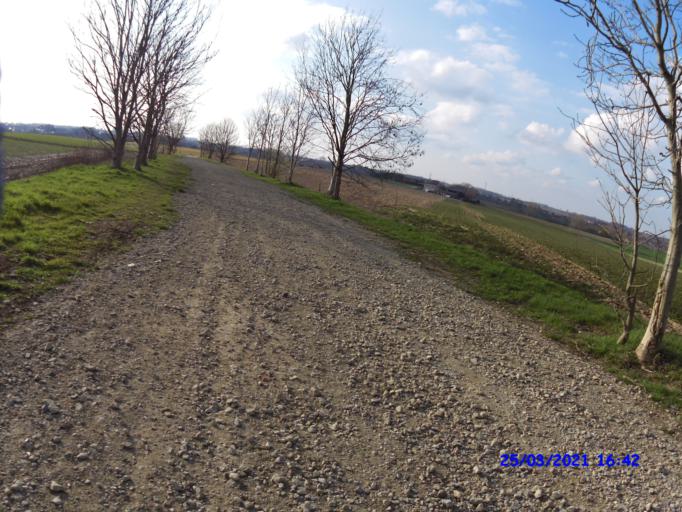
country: BE
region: Flanders
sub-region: Provincie Vlaams-Brabant
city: Wemmel
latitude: 50.8916
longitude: 4.2983
